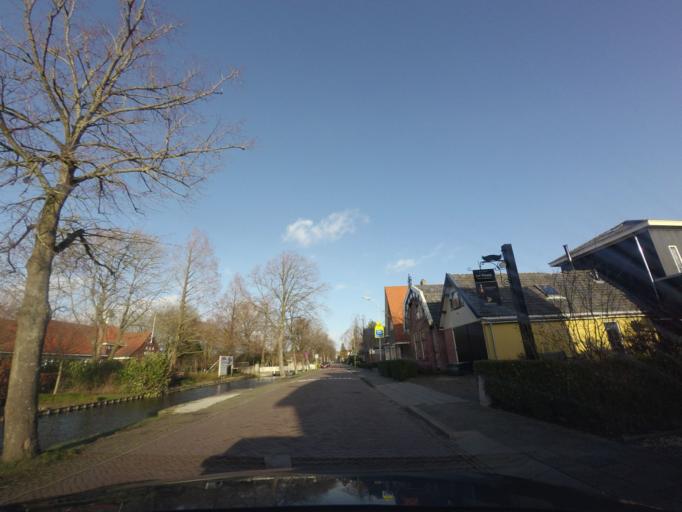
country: NL
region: North Holland
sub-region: Gemeente Opmeer
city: Opmeer
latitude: 52.7356
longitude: 4.8899
